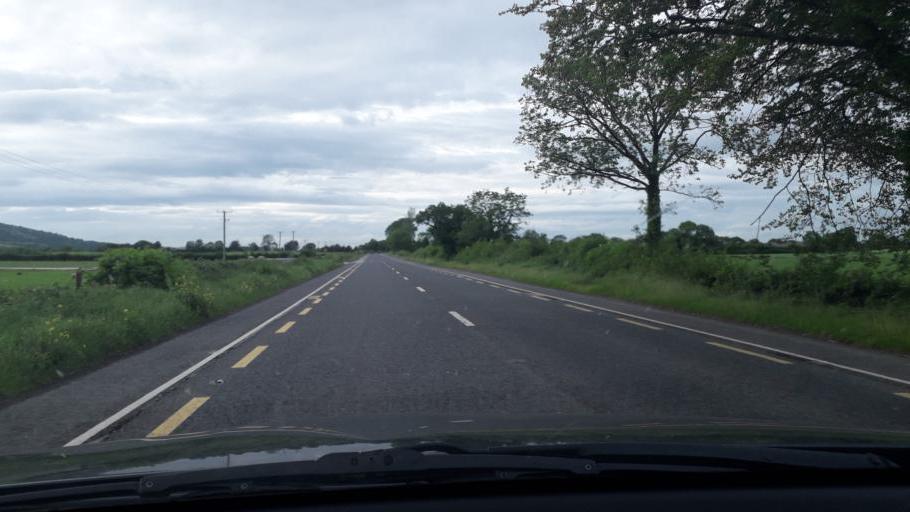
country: IE
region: Leinster
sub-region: County Carlow
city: Carlow
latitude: 52.7991
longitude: -6.9500
